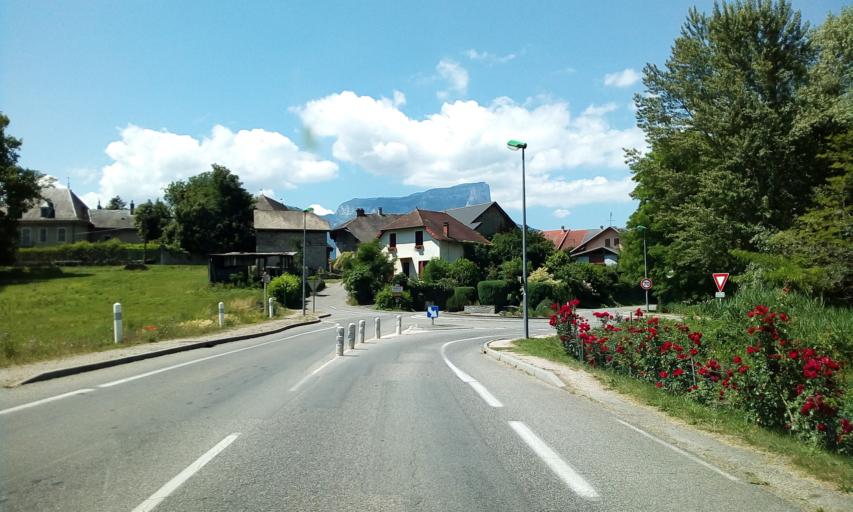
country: FR
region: Rhone-Alpes
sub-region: Departement de la Savoie
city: Montmelian
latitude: 45.5019
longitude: 6.0338
